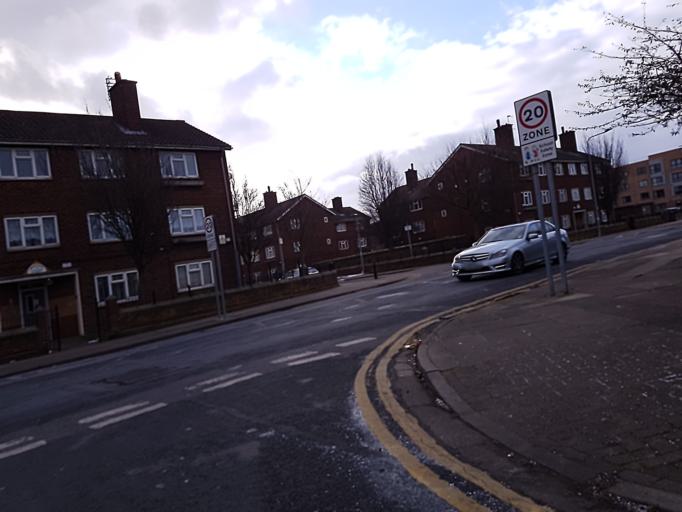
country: GB
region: England
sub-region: North East Lincolnshire
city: Grimsby
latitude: 53.5742
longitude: -0.0682
